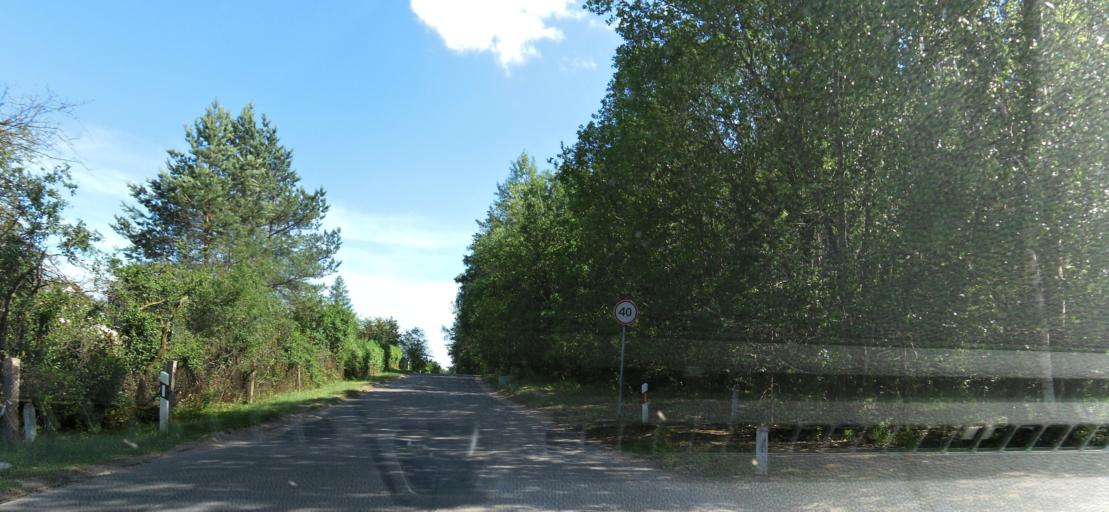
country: LT
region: Vilnius County
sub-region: Vilnius
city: Fabijoniskes
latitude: 54.8028
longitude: 25.3299
